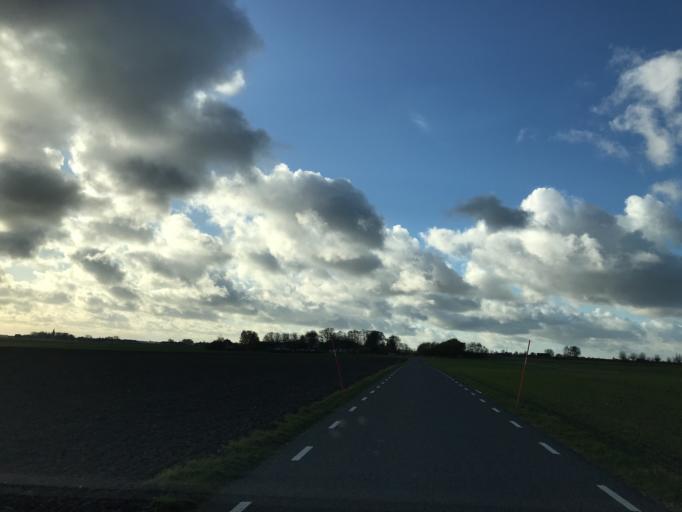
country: SE
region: Skane
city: Smygehamn
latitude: 55.3889
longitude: 13.4410
